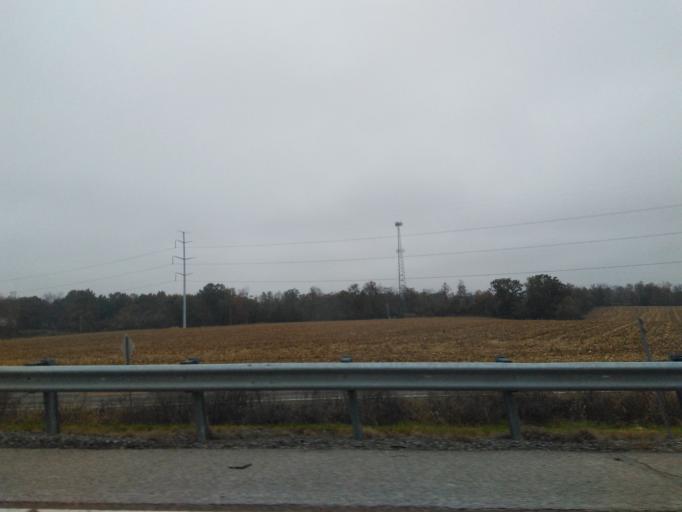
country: US
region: Illinois
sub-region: Madison County
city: Maryville
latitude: 38.7153
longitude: -89.9254
